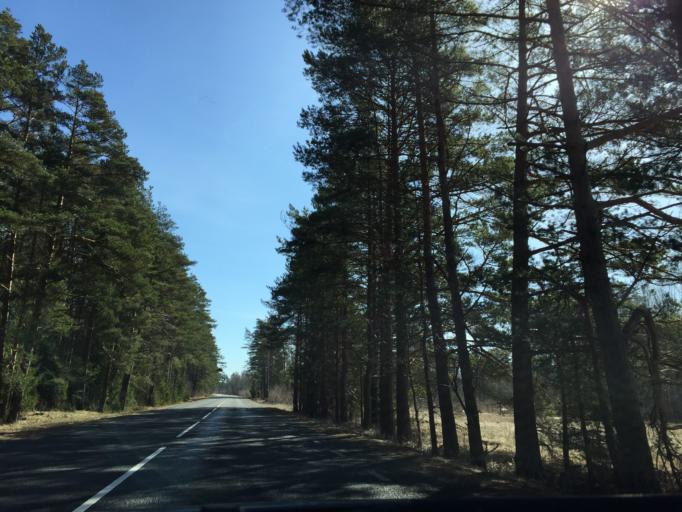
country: EE
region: Laeaene
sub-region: Lihula vald
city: Lihula
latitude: 58.5568
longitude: 23.8383
